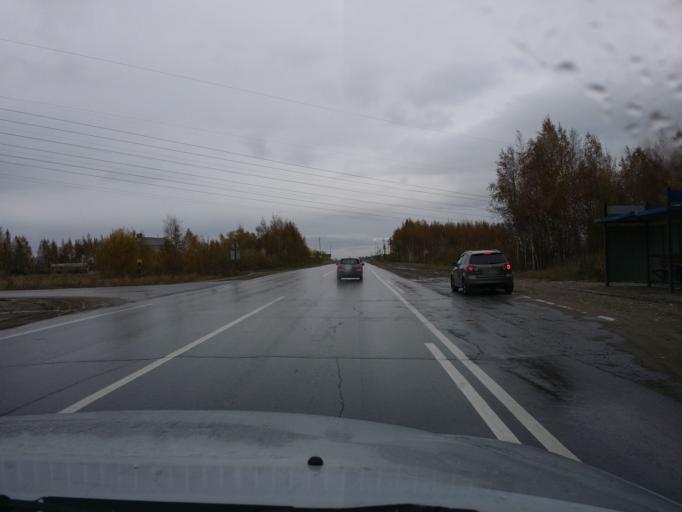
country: RU
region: Khanty-Mansiyskiy Avtonomnyy Okrug
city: Megion
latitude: 61.0513
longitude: 76.1124
